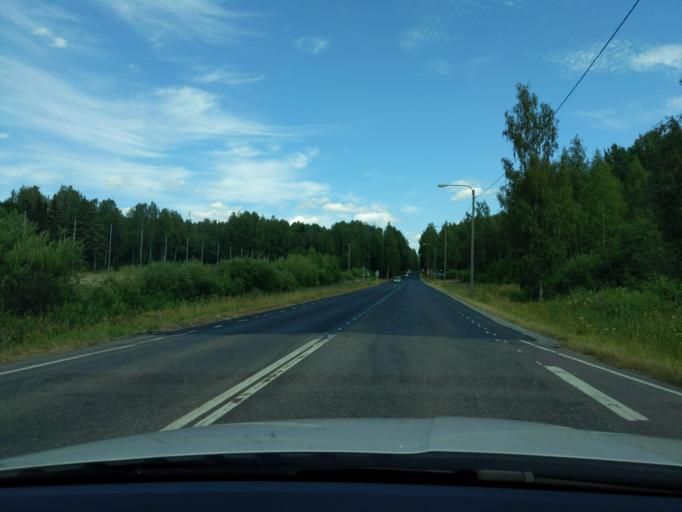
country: FI
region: Paijanne Tavastia
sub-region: Lahti
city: Lahti
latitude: 61.0261
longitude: 25.7292
